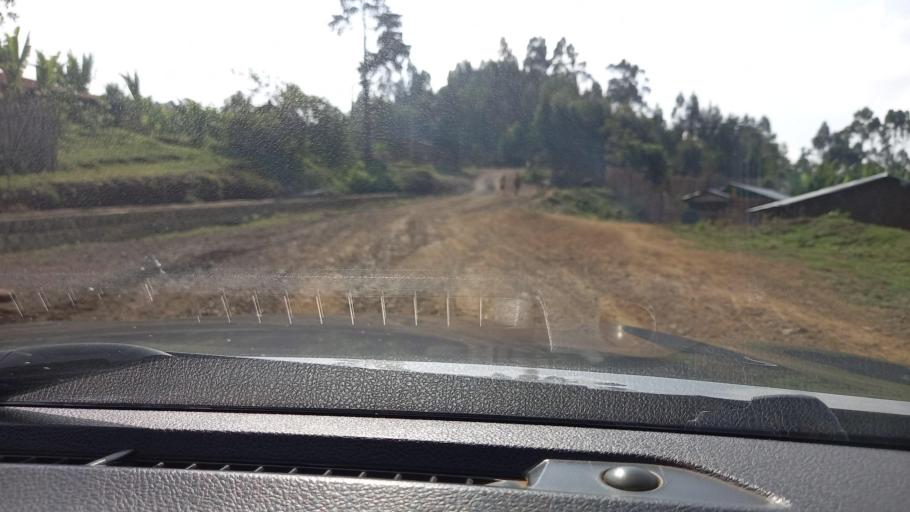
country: ET
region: Southern Nations, Nationalities, and People's Region
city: Mizan Teferi
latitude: 6.1630
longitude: 35.5943
